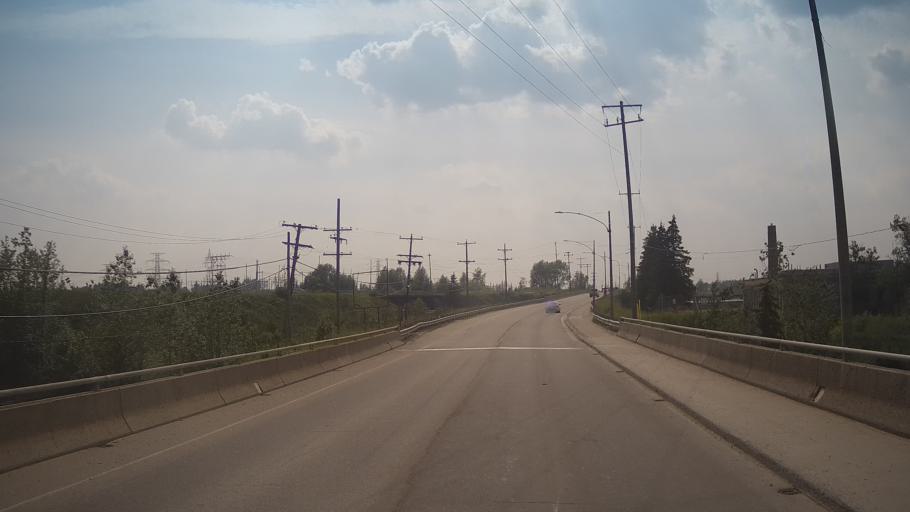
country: CA
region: Ontario
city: Kapuskasing
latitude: 49.4127
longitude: -82.4274
